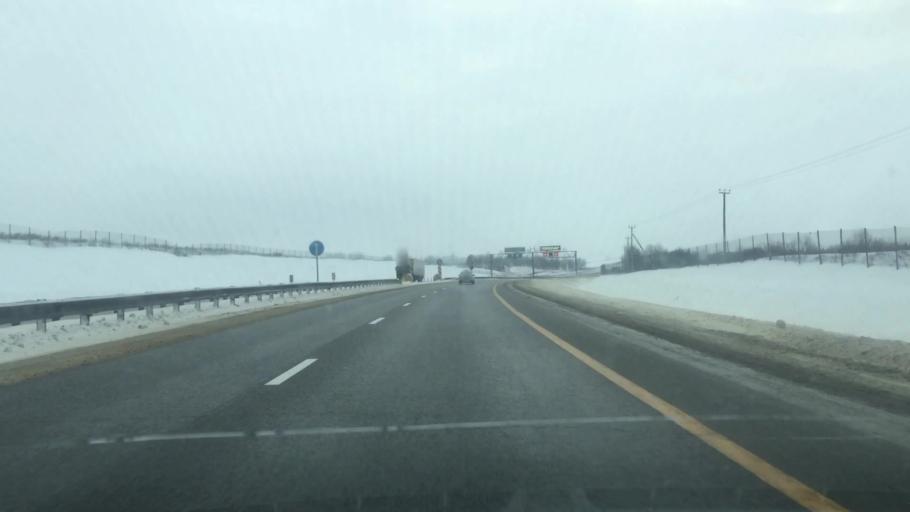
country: RU
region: Tula
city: Yefremov
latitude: 53.1387
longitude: 38.2447
